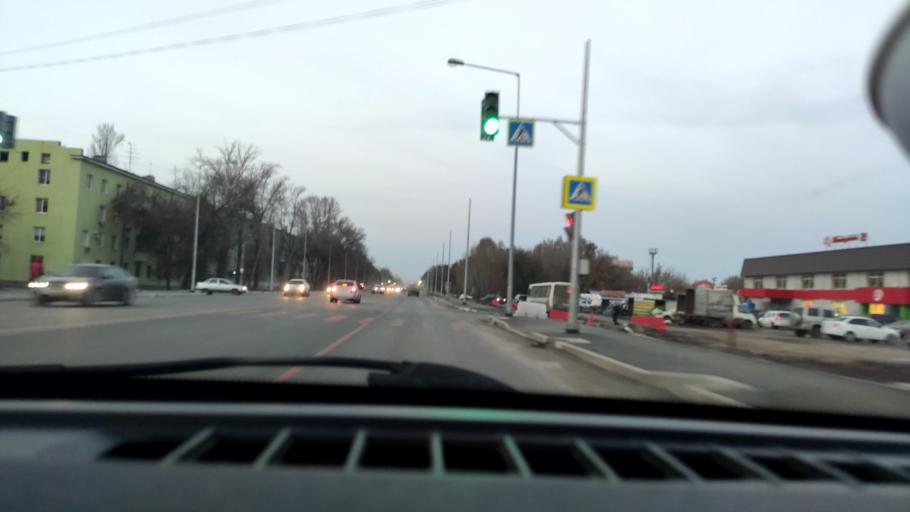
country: RU
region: Samara
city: Samara
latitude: 53.1147
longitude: 50.0842
